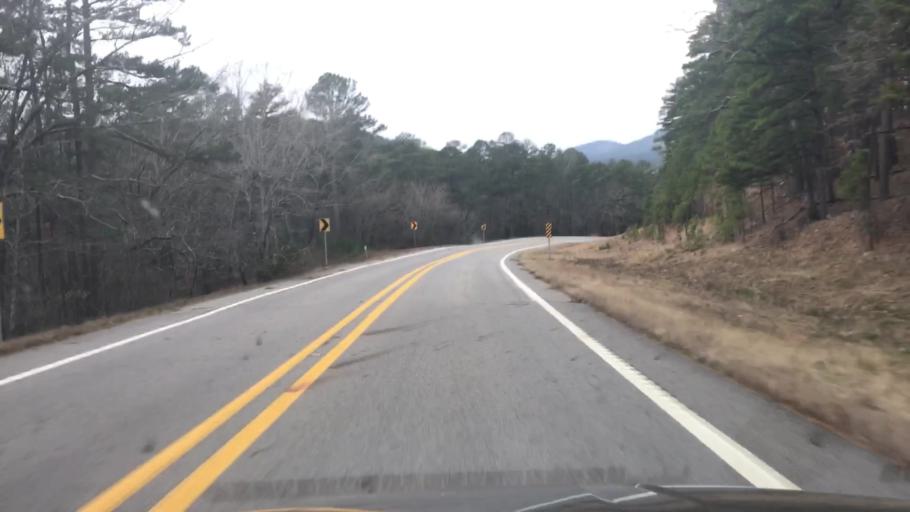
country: US
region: Arkansas
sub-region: Montgomery County
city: Mount Ida
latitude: 34.6836
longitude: -93.7998
